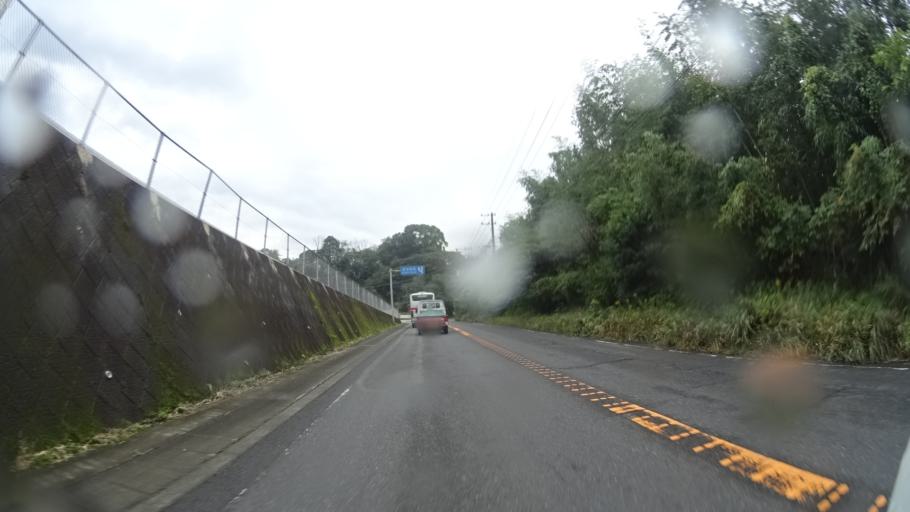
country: JP
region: Kagoshima
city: Kajiki
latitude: 31.7733
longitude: 130.6695
